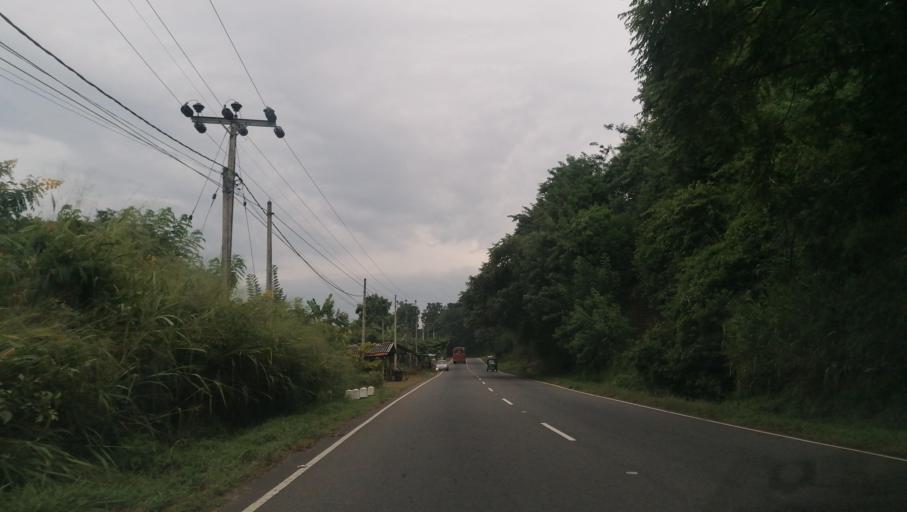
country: LK
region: Central
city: Kandy
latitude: 7.2450
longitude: 80.7258
